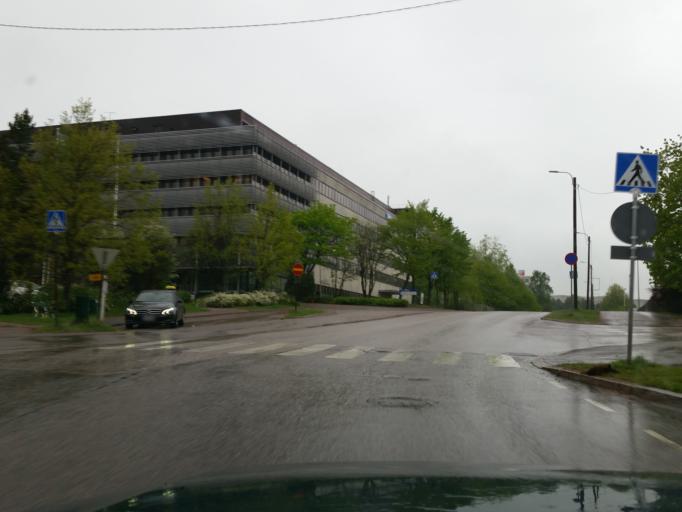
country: FI
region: Uusimaa
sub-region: Helsinki
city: Kauniainen
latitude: 60.2092
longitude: 24.7530
